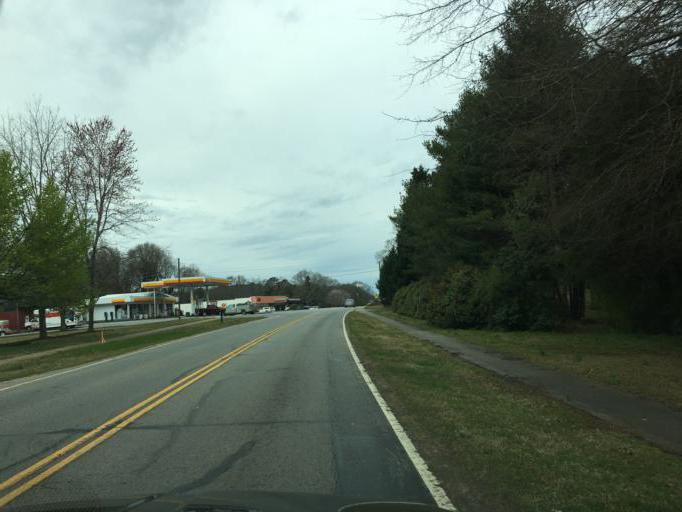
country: US
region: South Carolina
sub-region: Pickens County
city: Clemson
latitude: 34.6722
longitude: -82.8095
